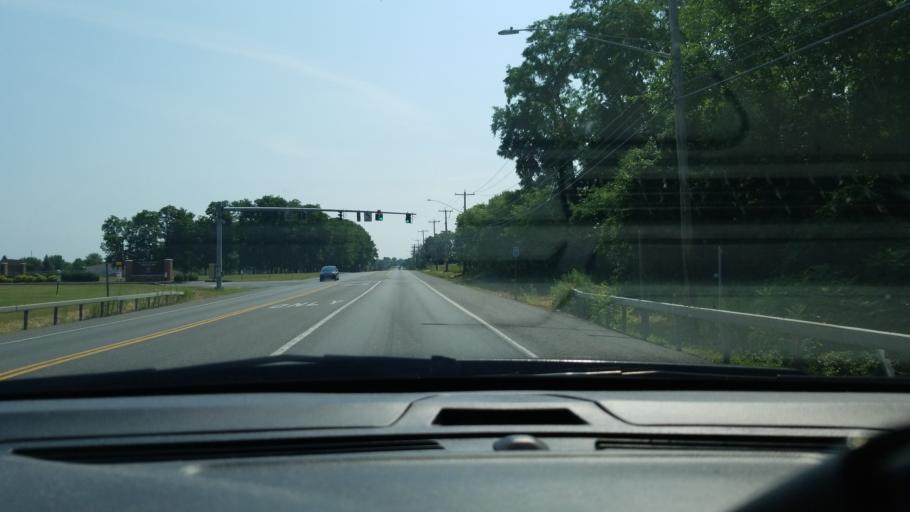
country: US
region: New York
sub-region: Onondaga County
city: Lyncourt
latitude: 43.0989
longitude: -76.1041
